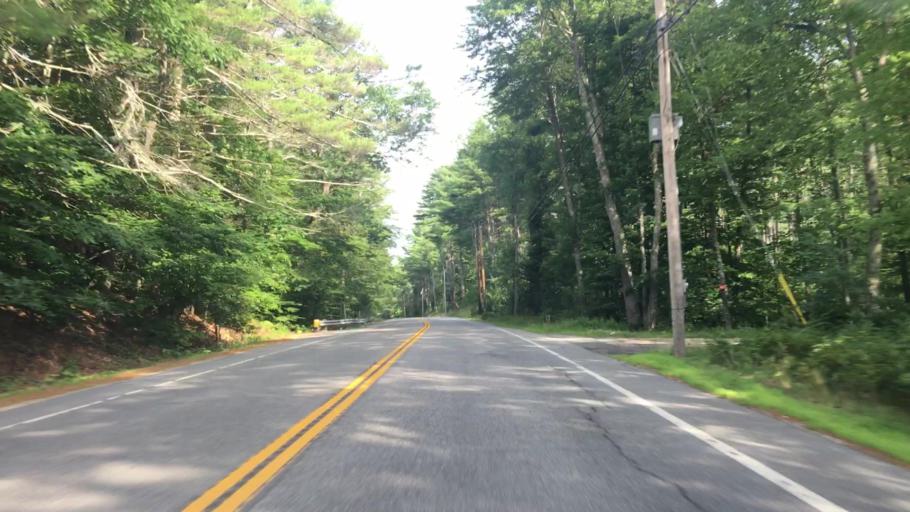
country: US
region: Maine
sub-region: York County
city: Limington
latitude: 43.7711
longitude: -70.7264
